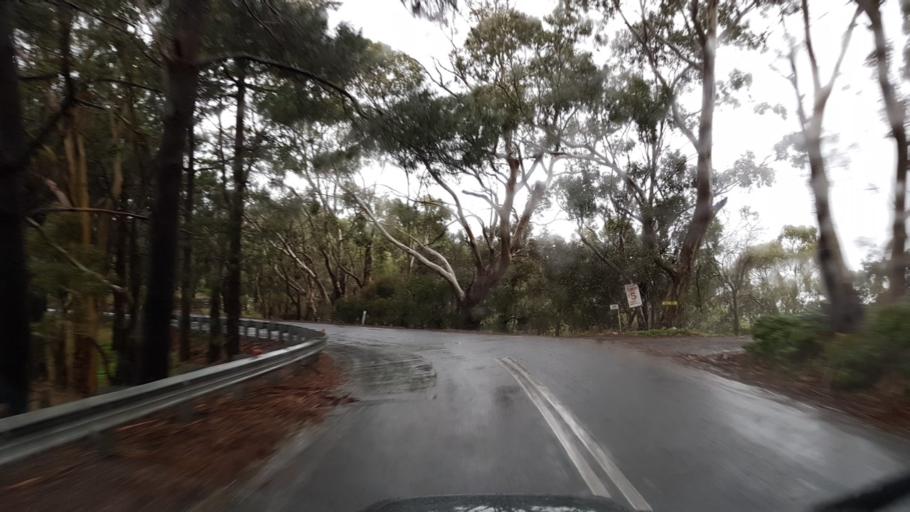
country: AU
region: South Australia
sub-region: Onkaparinga
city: Craigburn Farm
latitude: -35.0768
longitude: 138.6249
